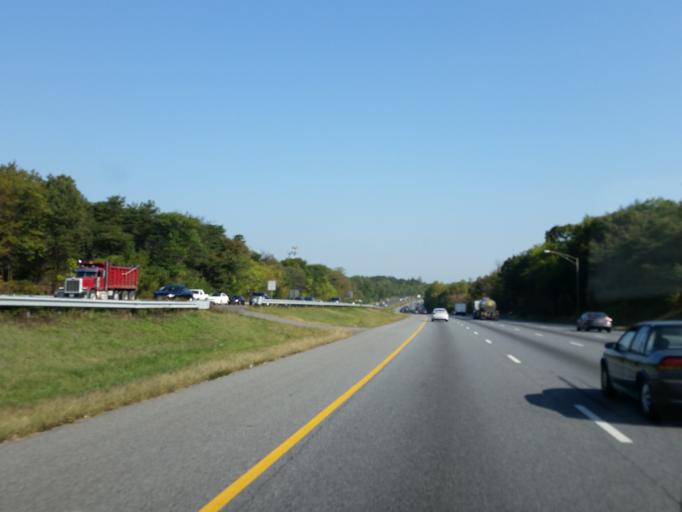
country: US
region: Maryland
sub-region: Prince George's County
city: Forestville
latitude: 38.8450
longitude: -76.8629
